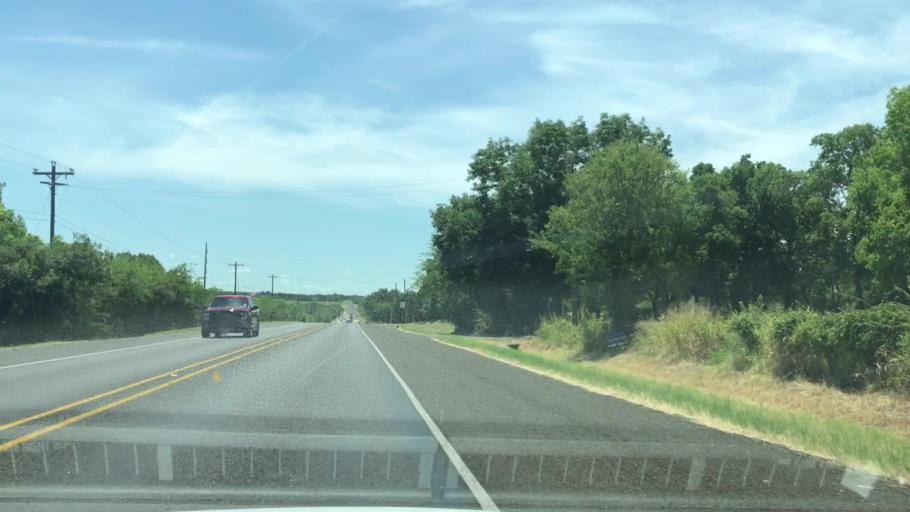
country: US
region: Texas
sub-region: Collin County
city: Lavon
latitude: 32.9911
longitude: -96.4668
